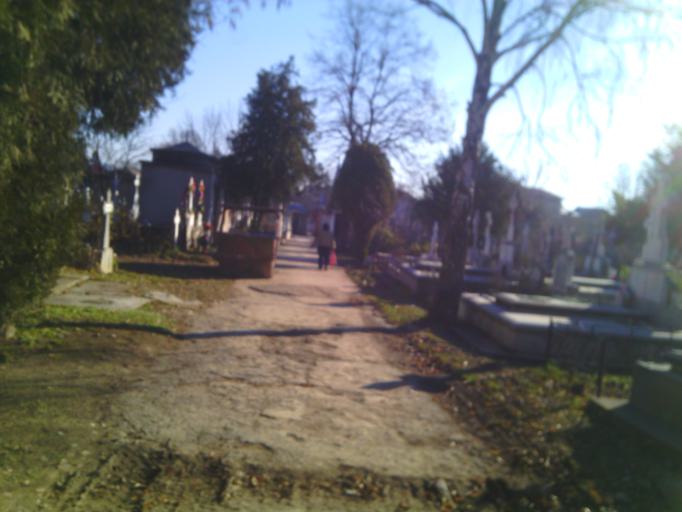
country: RO
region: Ilfov
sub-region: Comuna Popesti-Leordeni
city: Popesti-Leordeni
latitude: 44.3837
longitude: 26.1629
